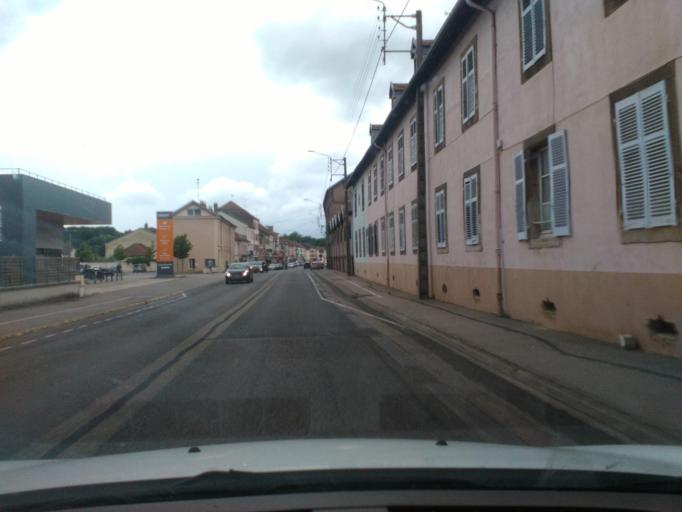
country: FR
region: Lorraine
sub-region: Departement de Meurthe-et-Moselle
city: Baccarat
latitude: 48.4473
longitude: 6.7434
